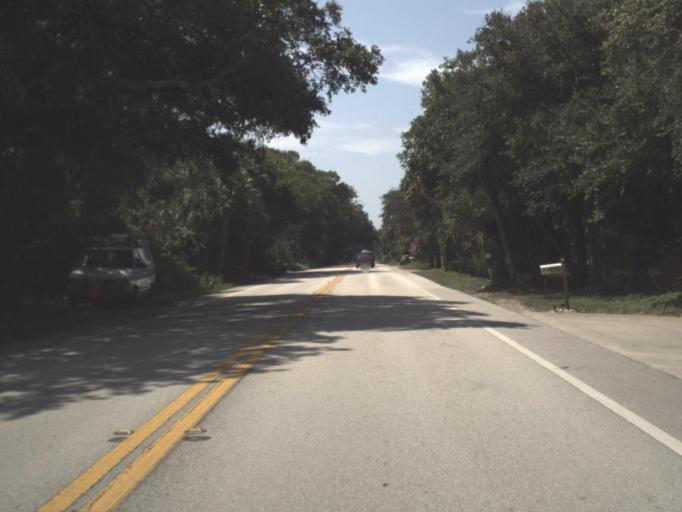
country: US
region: Florida
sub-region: Saint Johns County
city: Palm Valley
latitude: 30.1361
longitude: -81.3507
